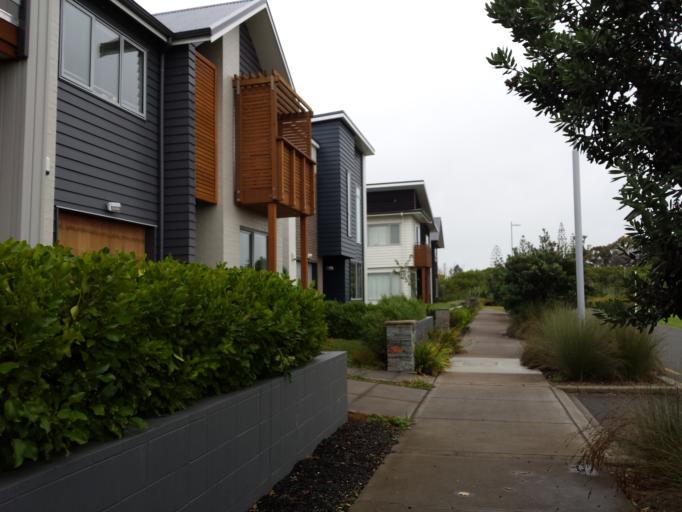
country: NZ
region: Auckland
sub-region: Auckland
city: Rosebank
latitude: -36.7909
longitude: 174.6576
